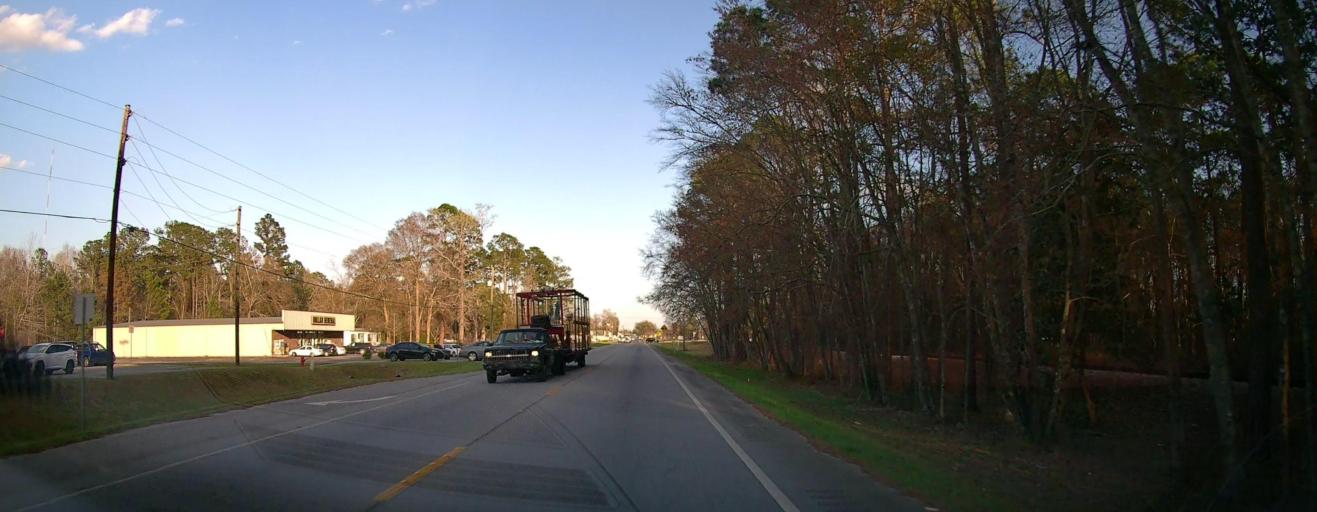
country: US
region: Georgia
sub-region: Bryan County
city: Pembroke
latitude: 32.1364
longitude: -81.6322
